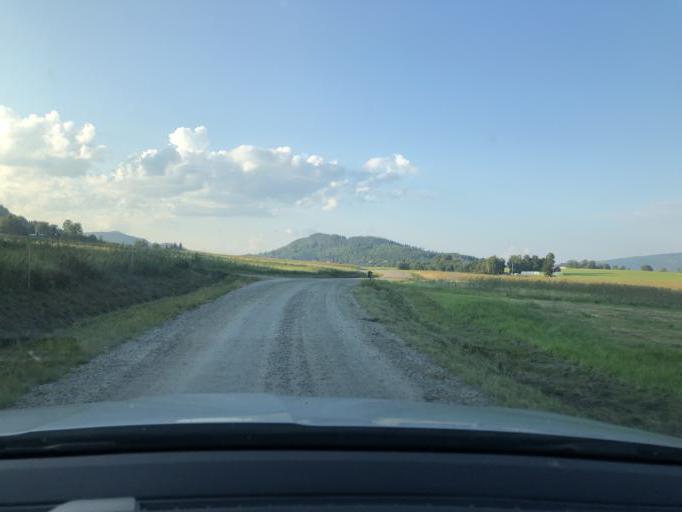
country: SE
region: Vaesternorrland
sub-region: Kramfors Kommun
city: Bollstabruk
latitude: 63.0691
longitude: 17.7341
